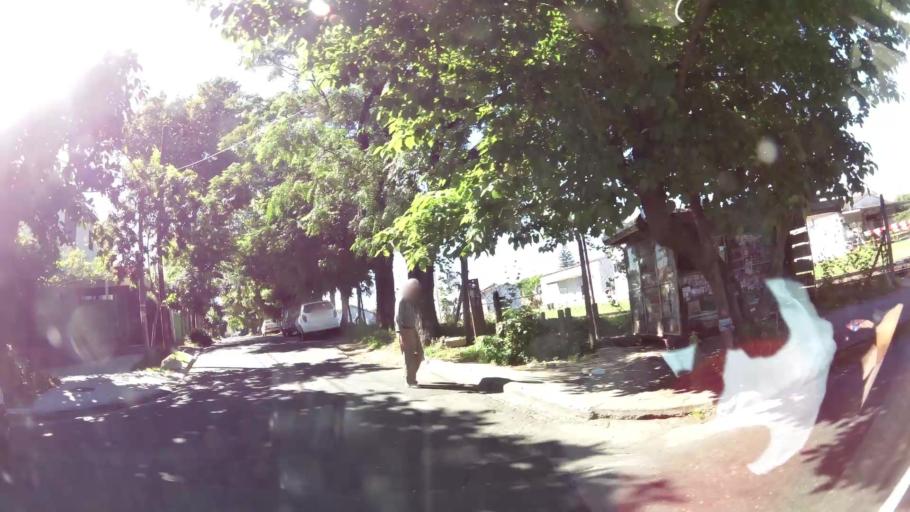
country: AR
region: Buenos Aires
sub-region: Partido de General San Martin
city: General San Martin
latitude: -34.5357
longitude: -58.5156
